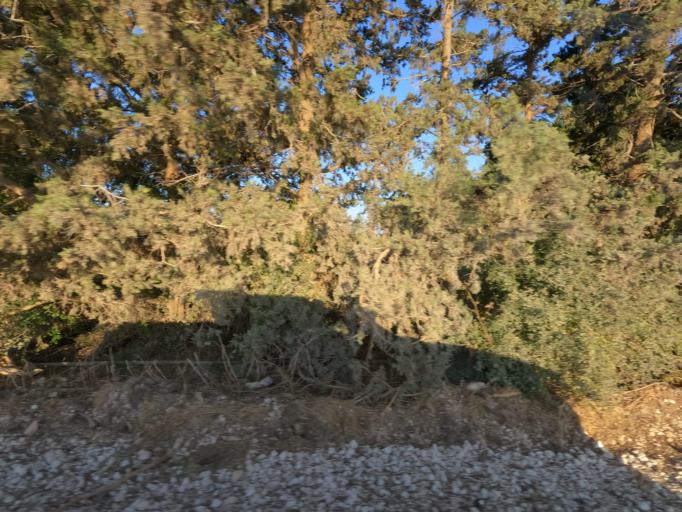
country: CY
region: Ammochostos
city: Achna
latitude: 35.0291
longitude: 33.7922
